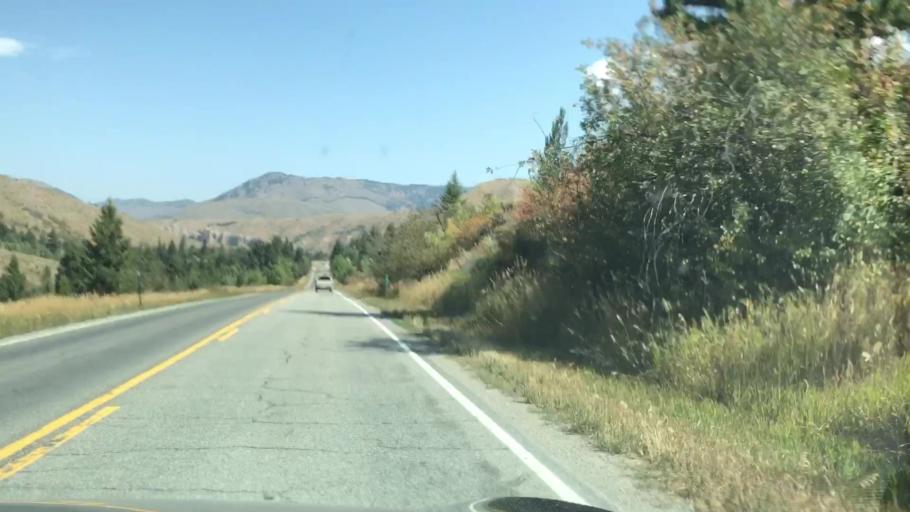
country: US
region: Wyoming
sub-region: Teton County
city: Hoback
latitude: 43.3330
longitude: -110.7269
